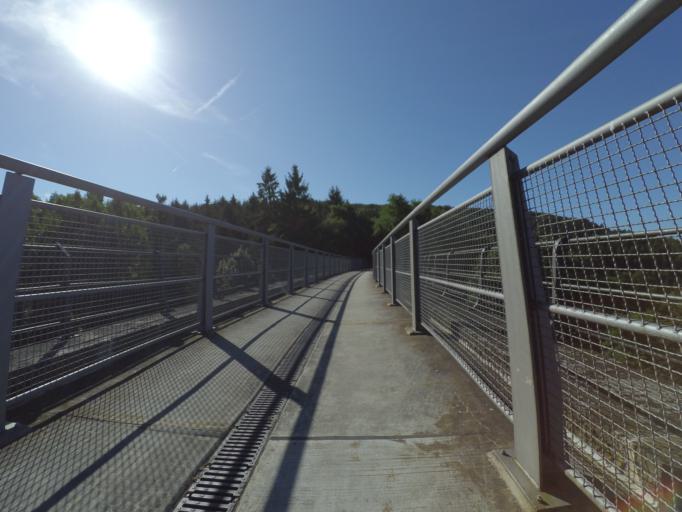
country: DE
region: Rheinland-Pfalz
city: Daun
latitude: 50.1948
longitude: 6.8405
